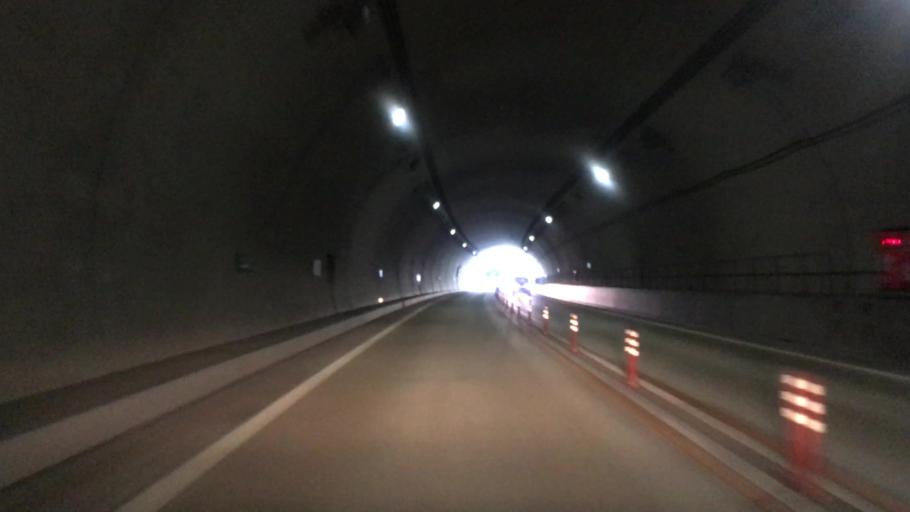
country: JP
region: Tottori
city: Tottori
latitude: 35.5663
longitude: 134.2893
